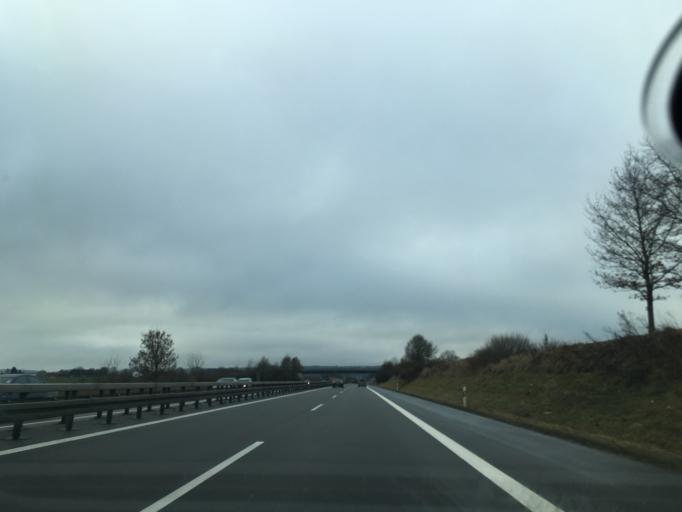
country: DE
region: Bavaria
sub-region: Swabia
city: Apfeltrach
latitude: 48.0294
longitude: 10.5080
